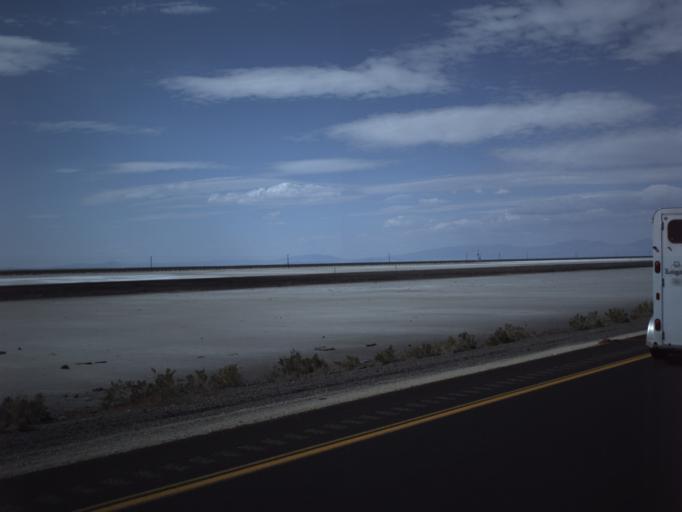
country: US
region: Utah
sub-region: Tooele County
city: Wendover
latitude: 40.7324
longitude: -113.5257
